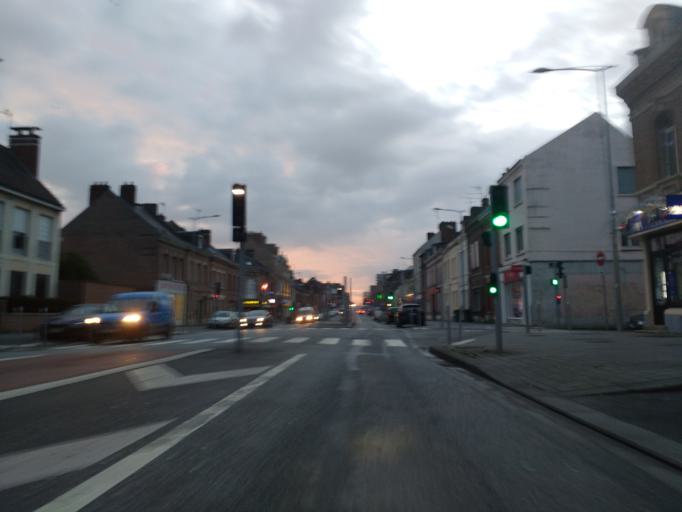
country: FR
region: Picardie
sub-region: Departement de la Somme
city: Rivery
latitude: 49.8873
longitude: 2.3151
